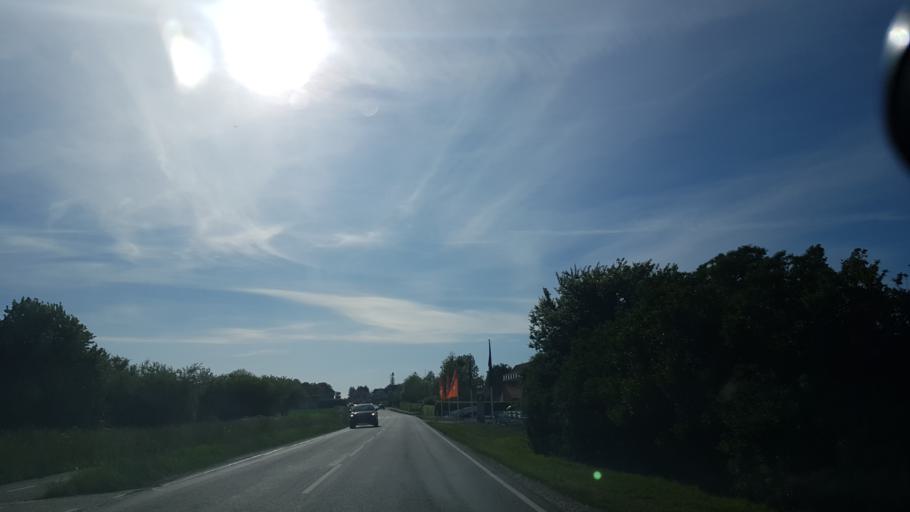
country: DK
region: Zealand
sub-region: Slagelse Kommune
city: Forlev
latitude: 55.4370
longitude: 11.2541
